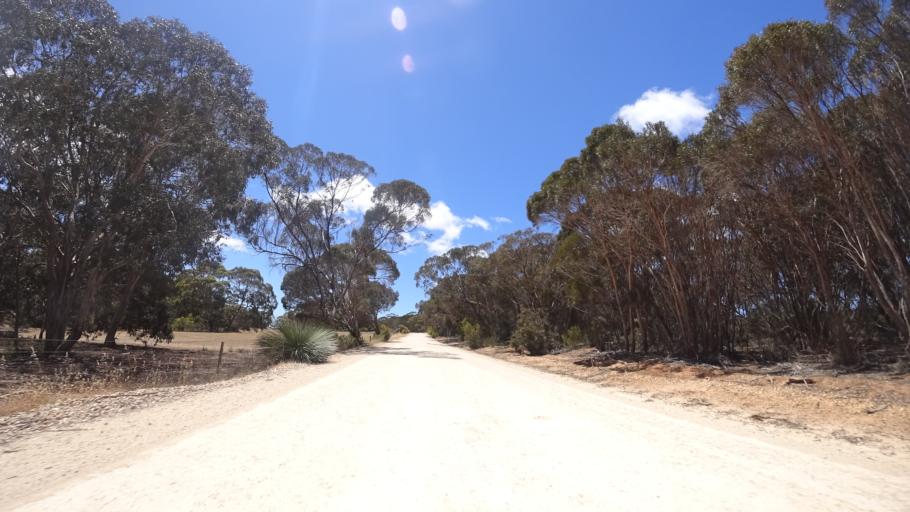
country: AU
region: South Australia
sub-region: Kangaroo Island
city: Kingscote
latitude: -35.8260
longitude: 138.0216
